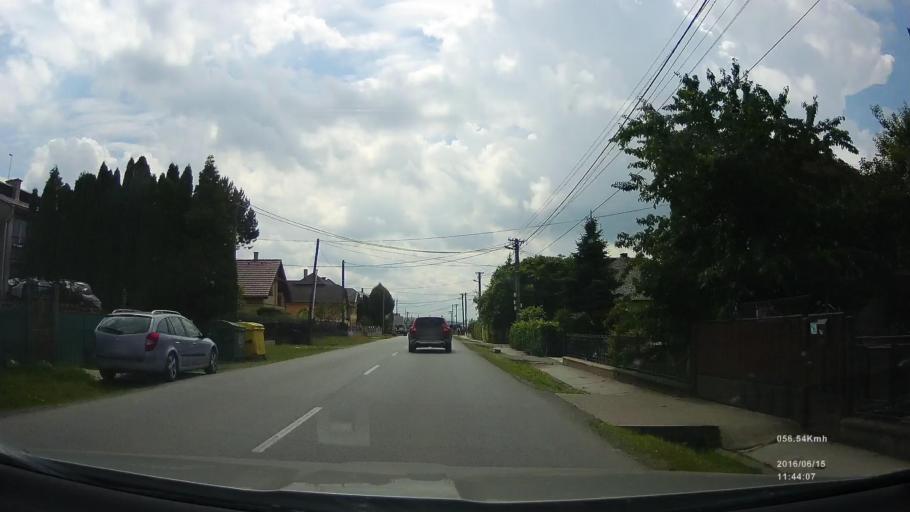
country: SK
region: Kosicky
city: Kosice
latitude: 48.7468
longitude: 21.3444
